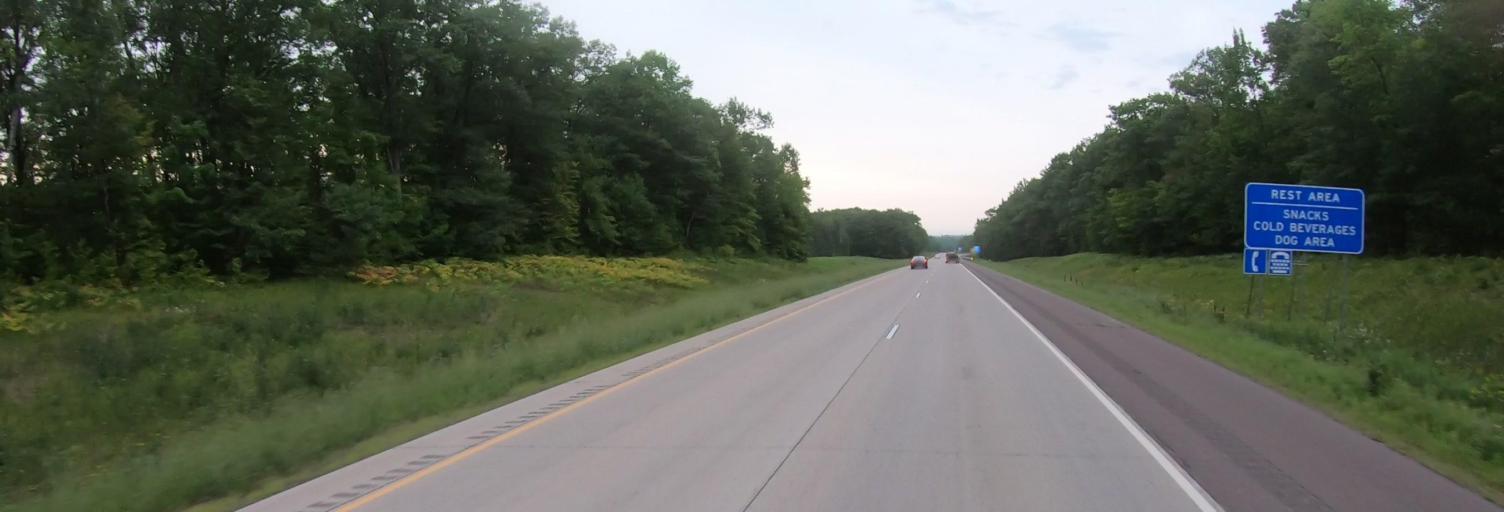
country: US
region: Minnesota
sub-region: Pine County
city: Sandstone
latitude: 46.2050
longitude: -92.8419
